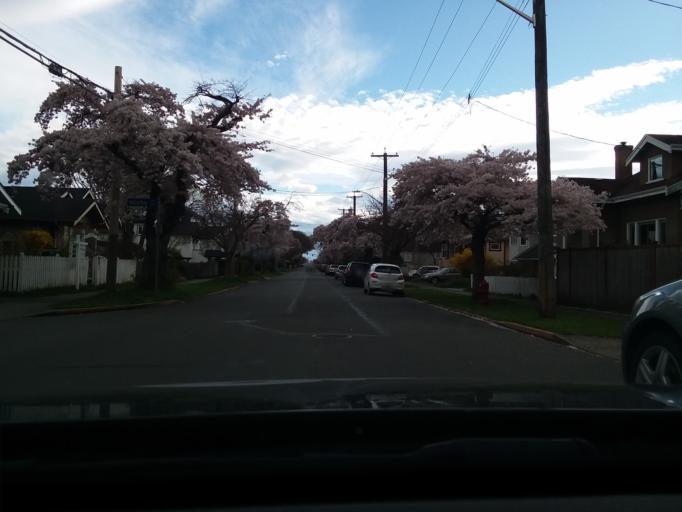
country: CA
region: British Columbia
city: Victoria
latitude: 48.4180
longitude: -123.3481
